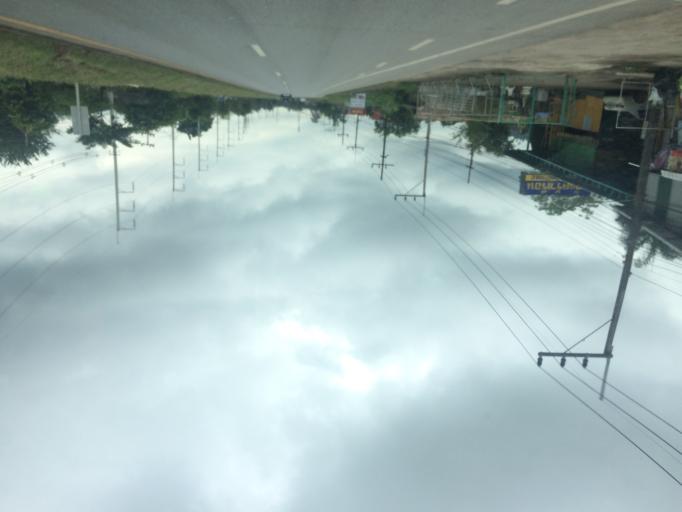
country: TH
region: Chiang Rai
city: Mae Chan
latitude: 20.0858
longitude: 99.8746
